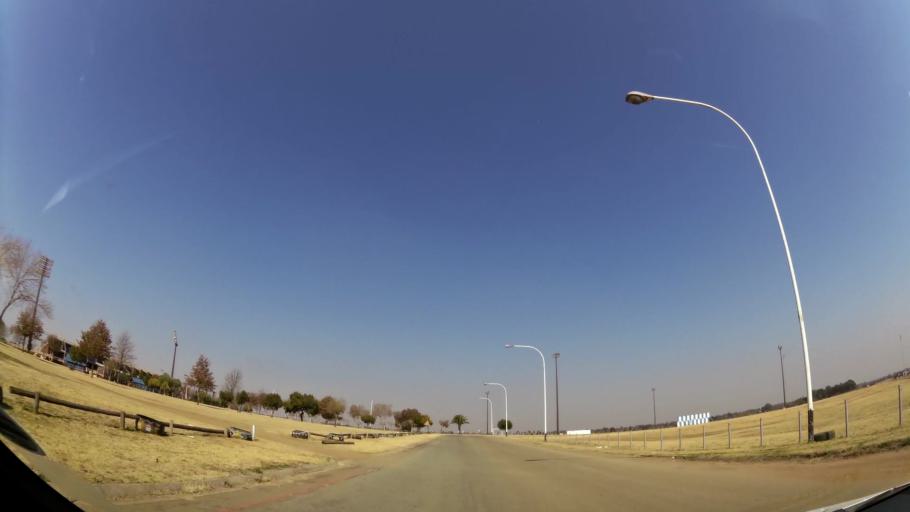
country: ZA
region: Gauteng
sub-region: Ekurhuleni Metropolitan Municipality
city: Boksburg
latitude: -26.2339
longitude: 28.2758
